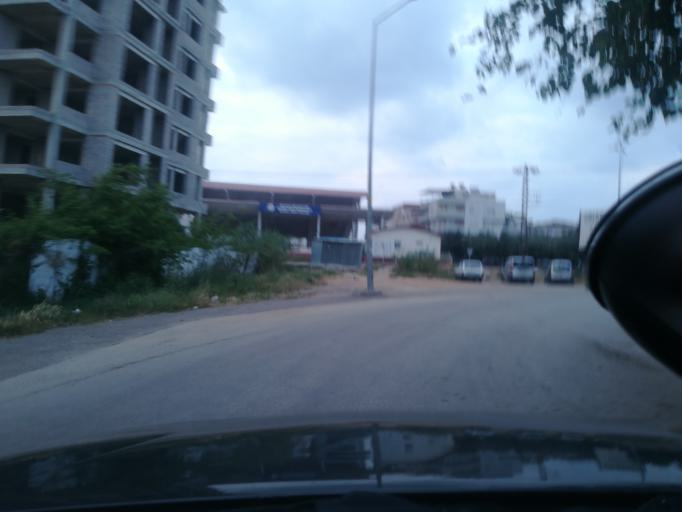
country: TR
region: Adana
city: Seyhan
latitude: 37.0170
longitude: 35.2705
